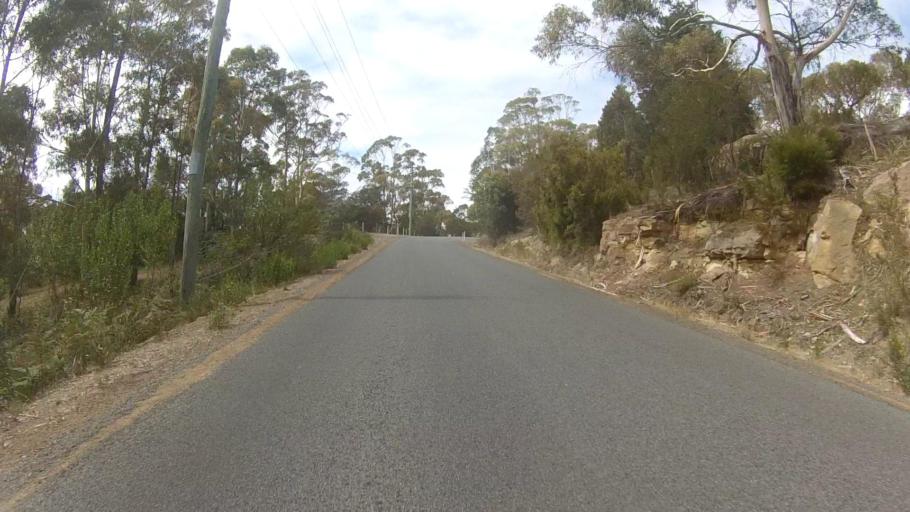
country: AU
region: Tasmania
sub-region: Kingborough
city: Blackmans Bay
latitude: -43.0200
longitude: 147.3211
